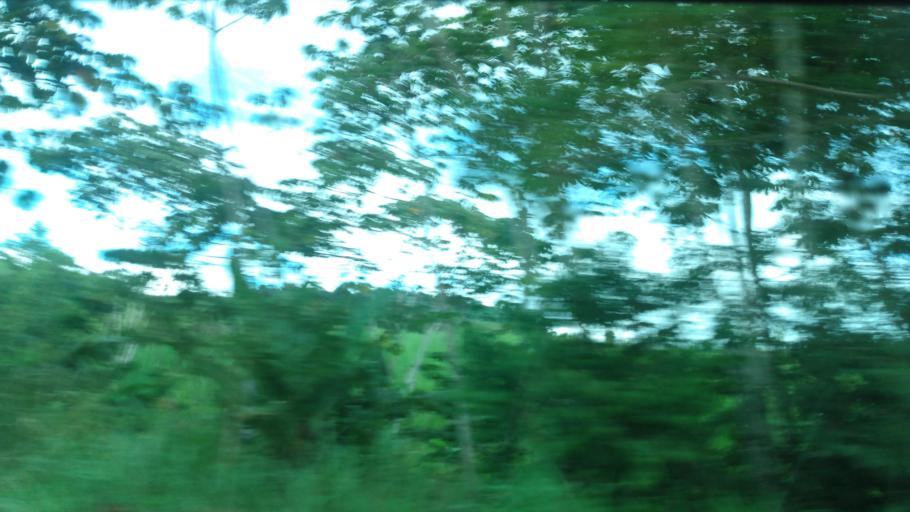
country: BR
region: Pernambuco
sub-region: Catende
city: Catende
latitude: -8.7125
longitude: -35.7721
